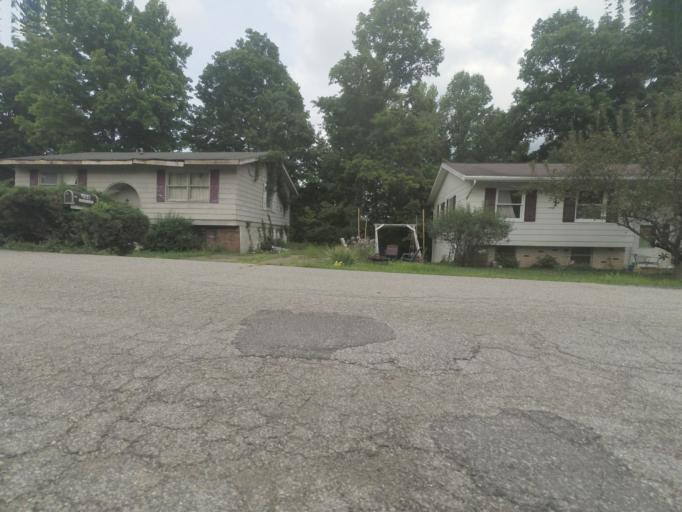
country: US
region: West Virginia
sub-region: Cabell County
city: Huntington
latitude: 38.3871
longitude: -82.4223
